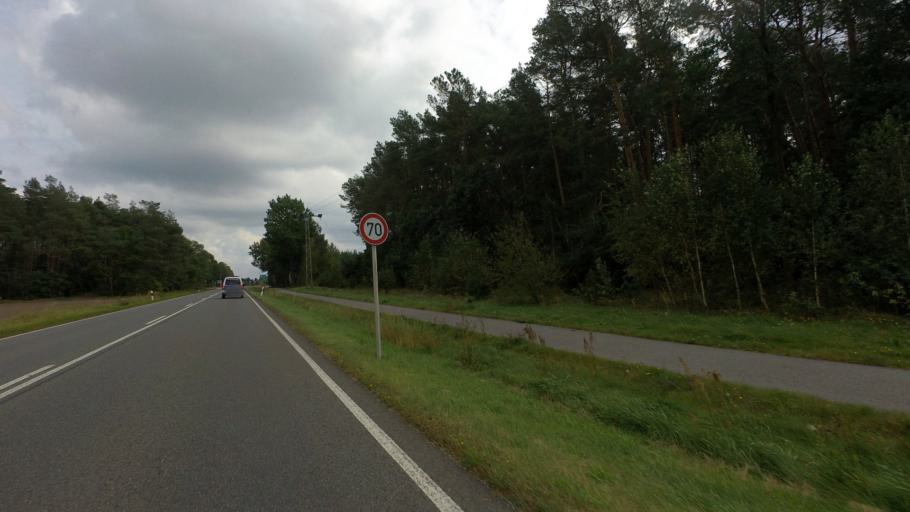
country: DE
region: Brandenburg
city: Sallgast
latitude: 51.6132
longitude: 13.8407
